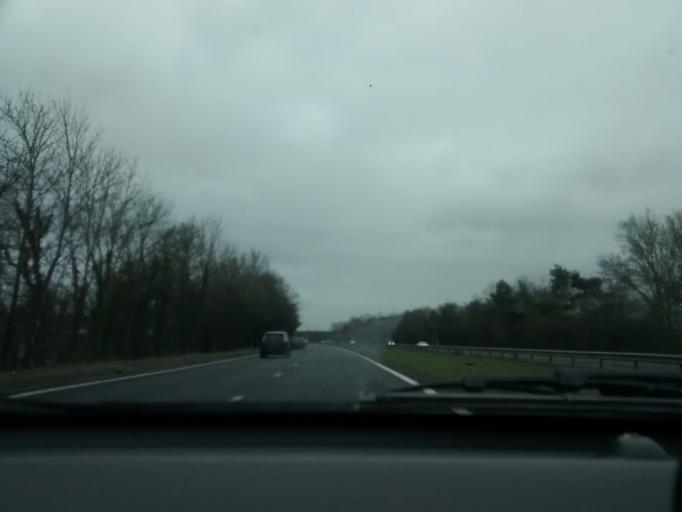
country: GB
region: England
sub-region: Suffolk
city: Bramford
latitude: 52.1210
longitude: 1.1004
